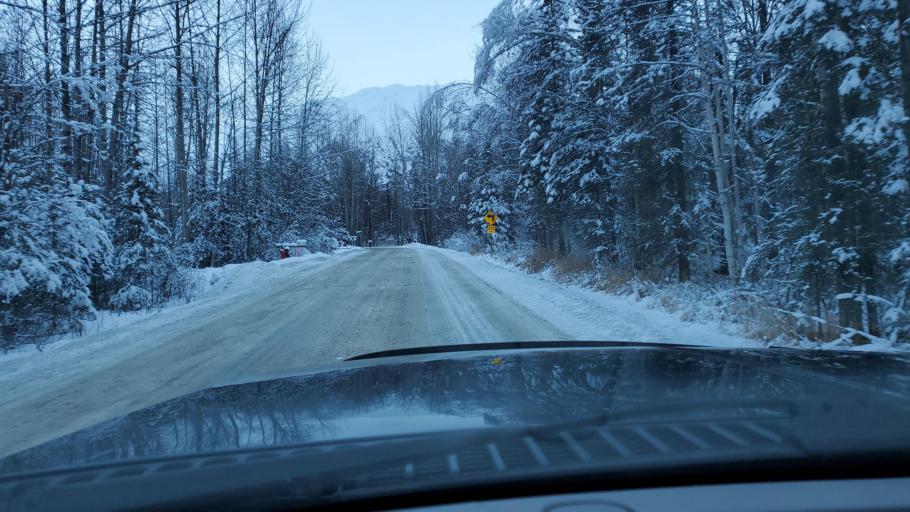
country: US
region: Alaska
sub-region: Matanuska-Susitna Borough
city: Fishhook
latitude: 61.6923
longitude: -149.2998
